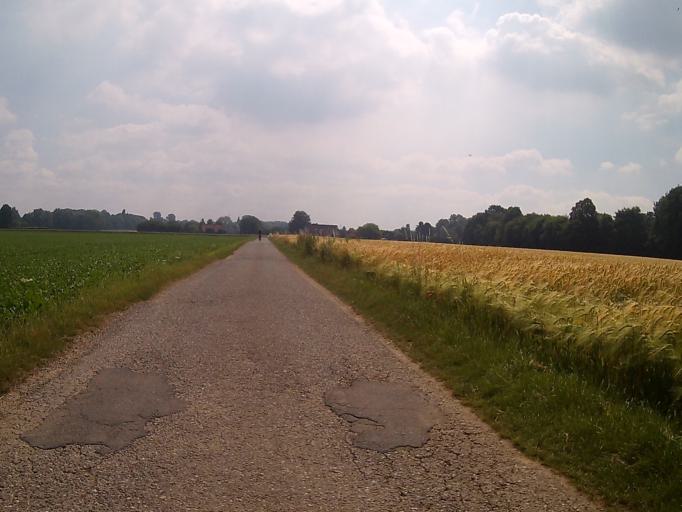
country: DE
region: North Rhine-Westphalia
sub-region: Regierungsbezirk Dusseldorf
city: Krefeld
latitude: 51.3812
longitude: 6.5704
